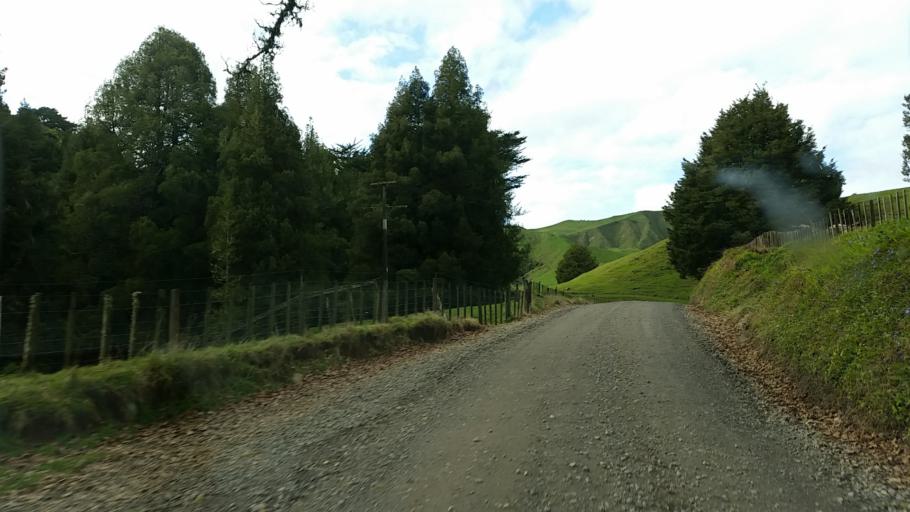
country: NZ
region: Taranaki
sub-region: New Plymouth District
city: Waitara
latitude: -39.1612
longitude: 174.5860
